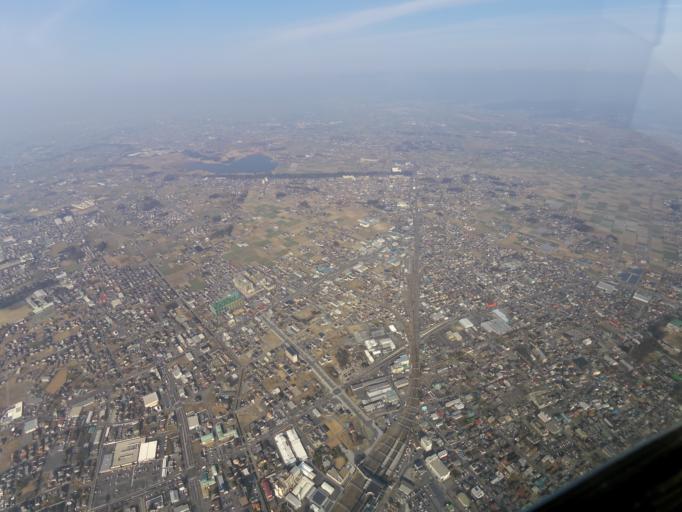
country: JP
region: Gunma
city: Tatebayashi
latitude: 36.2437
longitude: 139.5306
